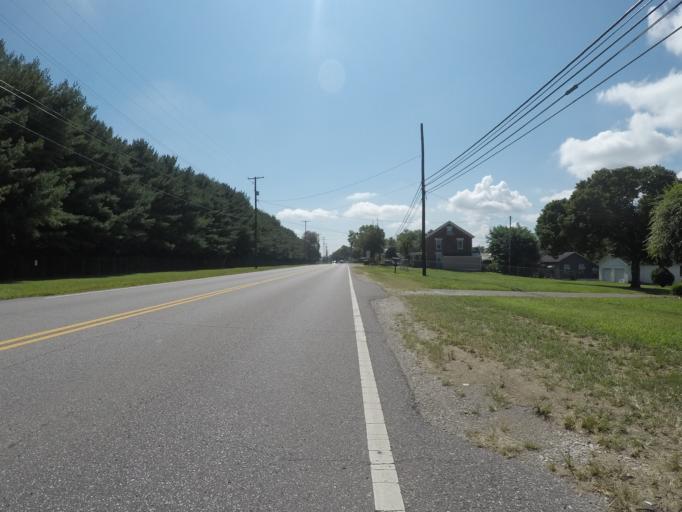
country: US
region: Ohio
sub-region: Lawrence County
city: South Point
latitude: 38.4299
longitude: -82.5936
